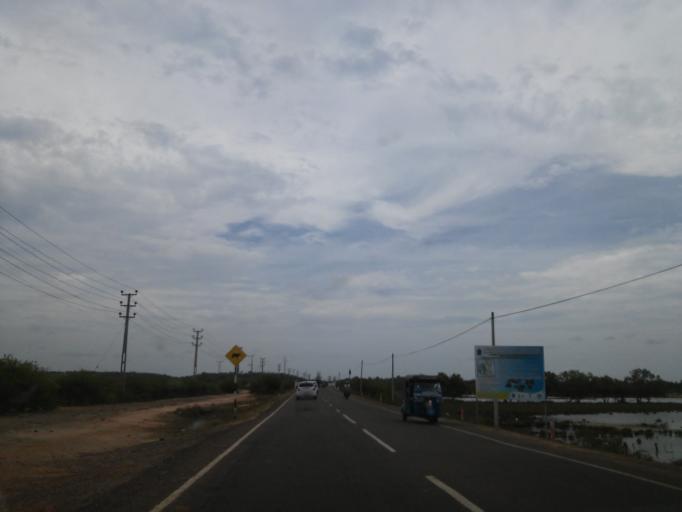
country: LK
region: Eastern Province
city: Trincomalee
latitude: 8.6200
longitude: 81.2092
